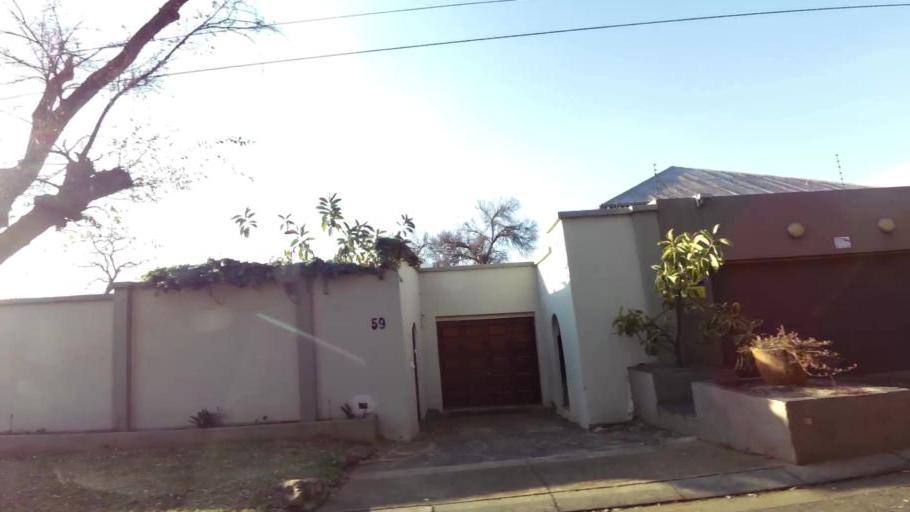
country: ZA
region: Gauteng
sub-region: City of Johannesburg Metropolitan Municipality
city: Johannesburg
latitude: -26.1749
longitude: 28.0081
